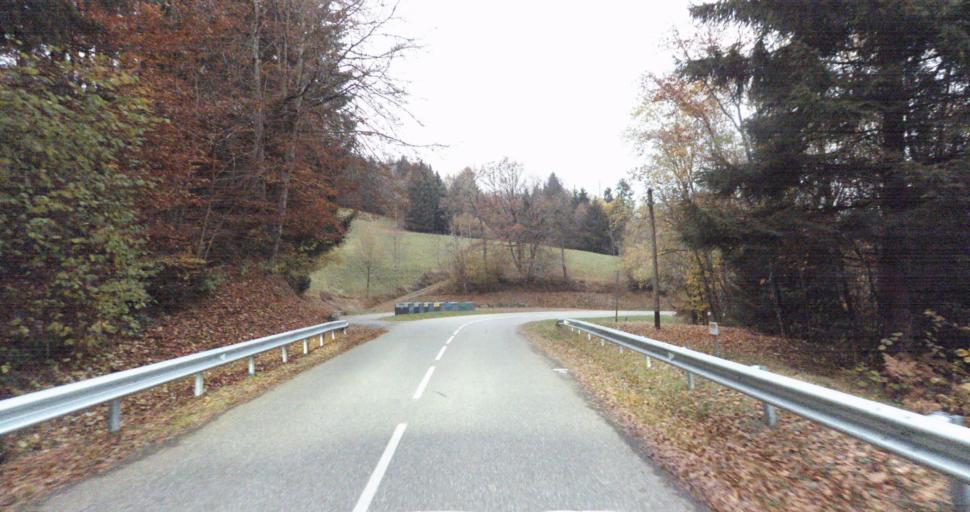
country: FR
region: Rhone-Alpes
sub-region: Departement de la Haute-Savoie
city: Saint-Jorioz
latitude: 45.7949
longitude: 6.1364
